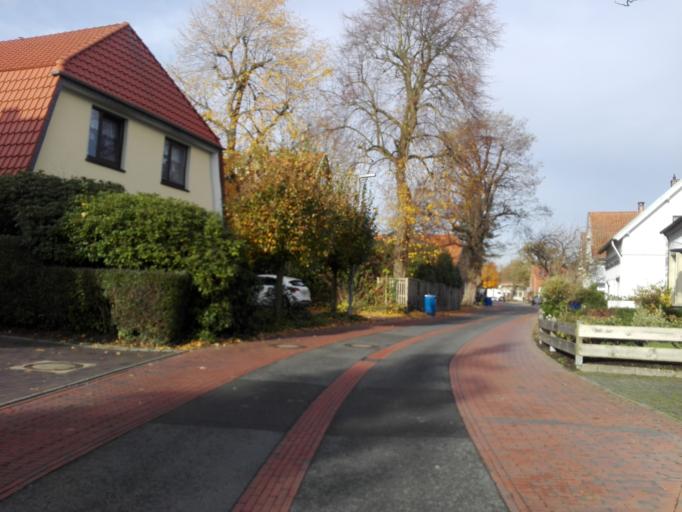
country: DE
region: Lower Saxony
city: Rastede
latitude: 53.2485
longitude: 8.1960
